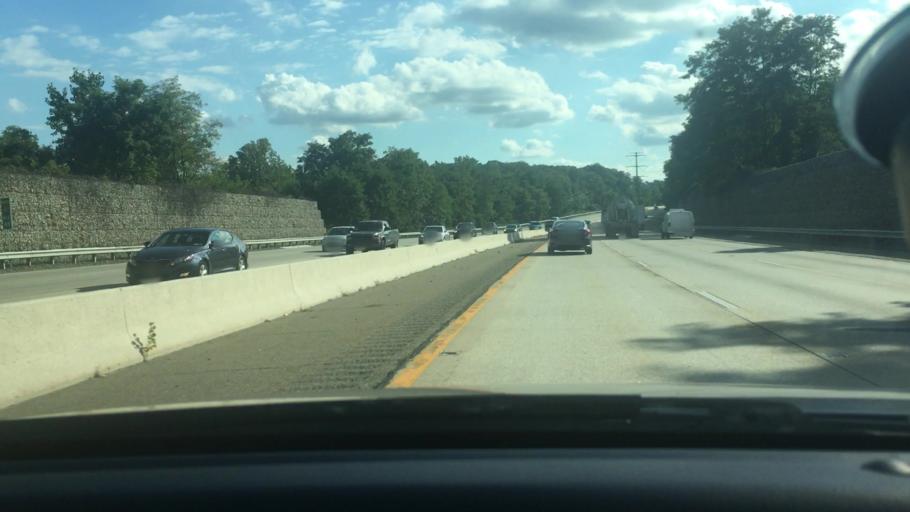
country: US
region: New Jersey
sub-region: Morris County
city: Boonton
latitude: 40.9259
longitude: -74.3596
